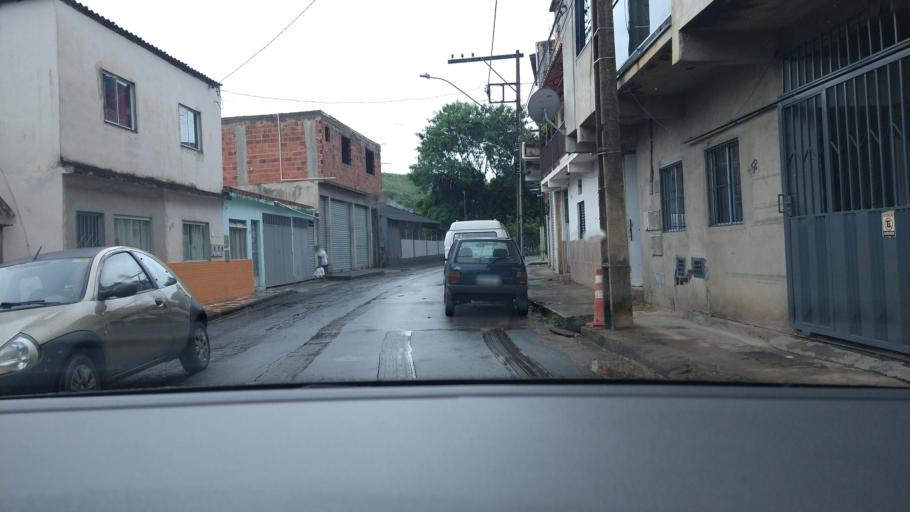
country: BR
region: Minas Gerais
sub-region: Ponte Nova
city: Ponte Nova
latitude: -20.4019
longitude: -42.9005
